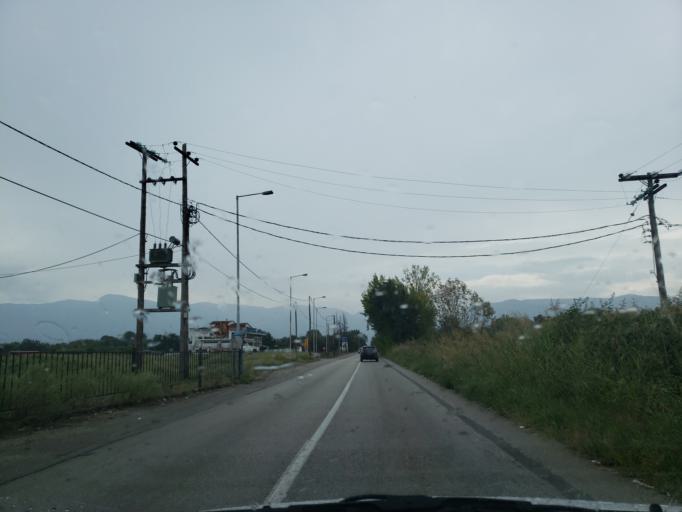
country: GR
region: Central Greece
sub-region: Nomos Fthiotidos
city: Anthili
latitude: 38.8534
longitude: 22.4404
